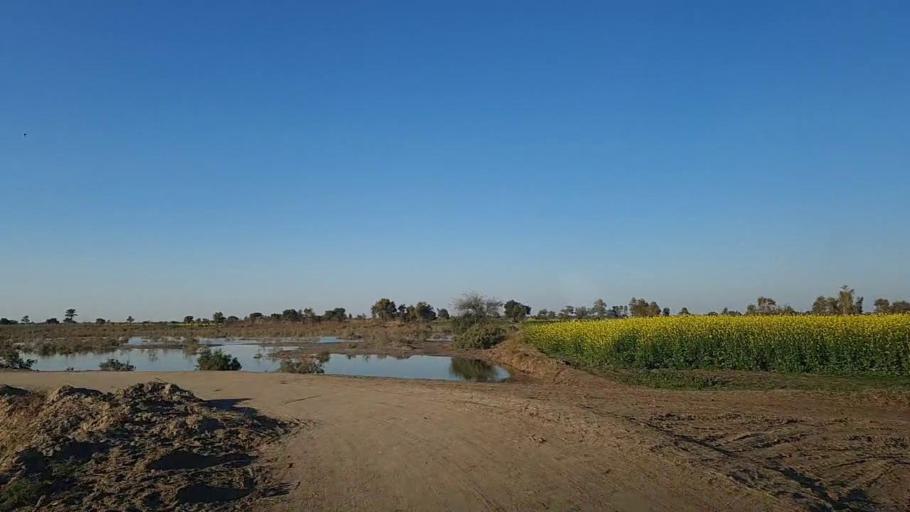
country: PK
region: Sindh
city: Sanghar
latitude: 26.1478
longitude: 68.9265
